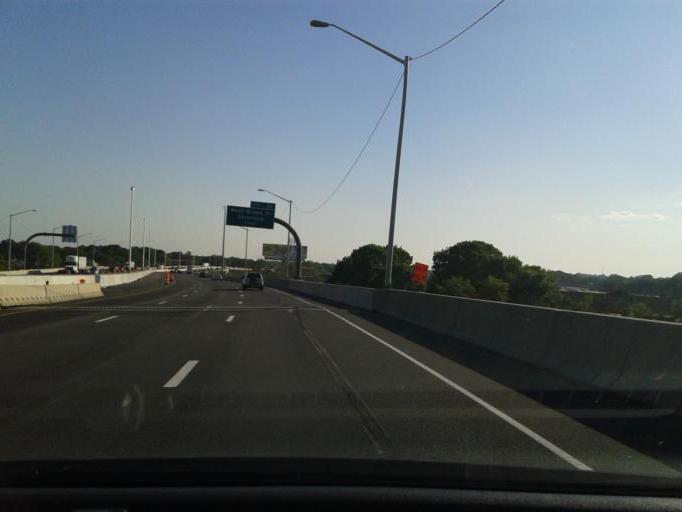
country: US
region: Connecticut
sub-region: Fairfield County
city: Stratford
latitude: 41.2032
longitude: -73.1143
